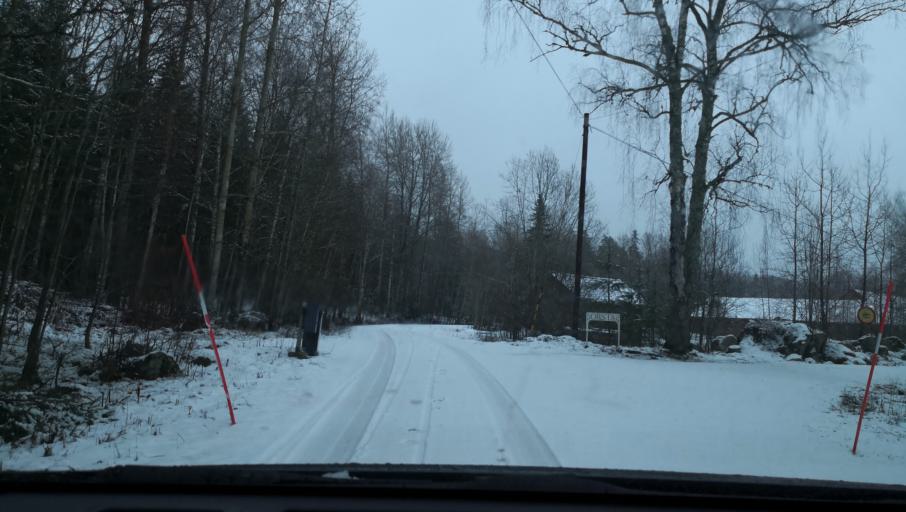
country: SE
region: Vaestmanland
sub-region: Kopings Kommun
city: Kolsva
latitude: 59.5640
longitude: 15.7867
